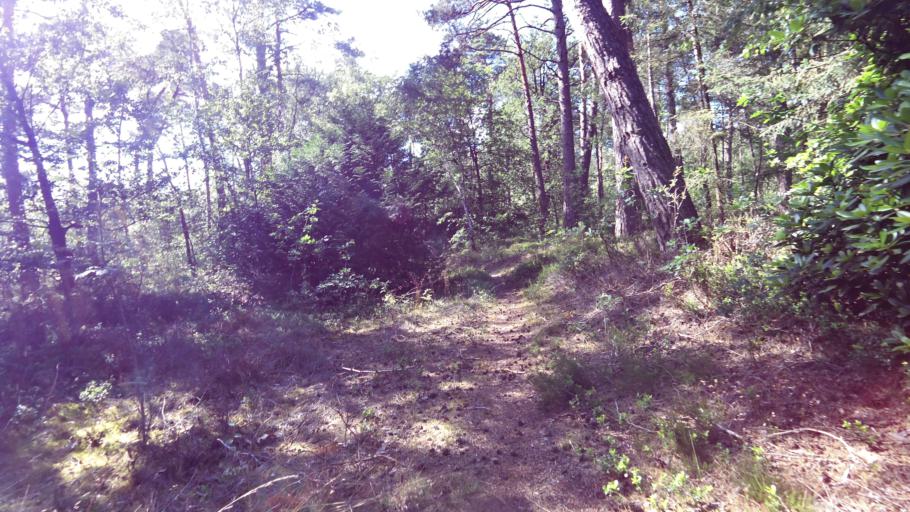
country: NL
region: Gelderland
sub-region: Gemeente Epe
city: Vaassen
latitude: 52.2683
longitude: 5.9284
